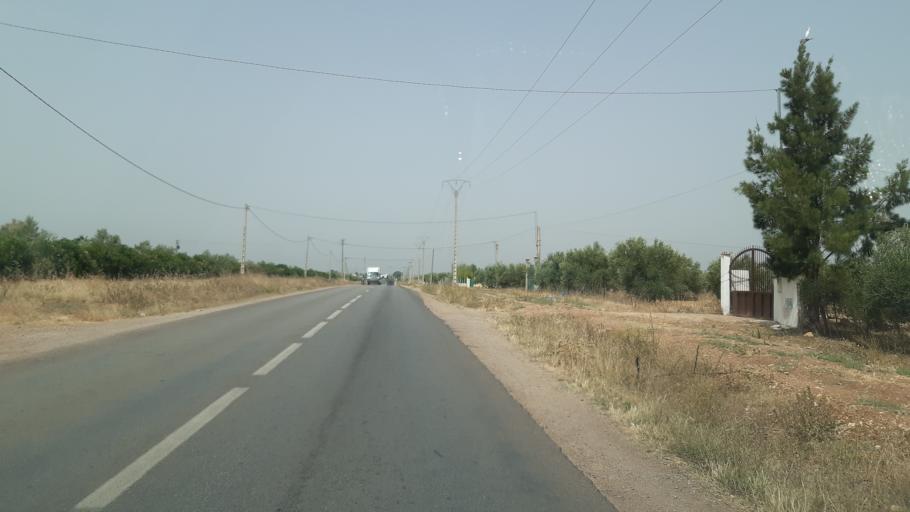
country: MA
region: Fes-Boulemane
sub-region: Fes
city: Oulad Tayeb
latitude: 33.8963
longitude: -5.0172
